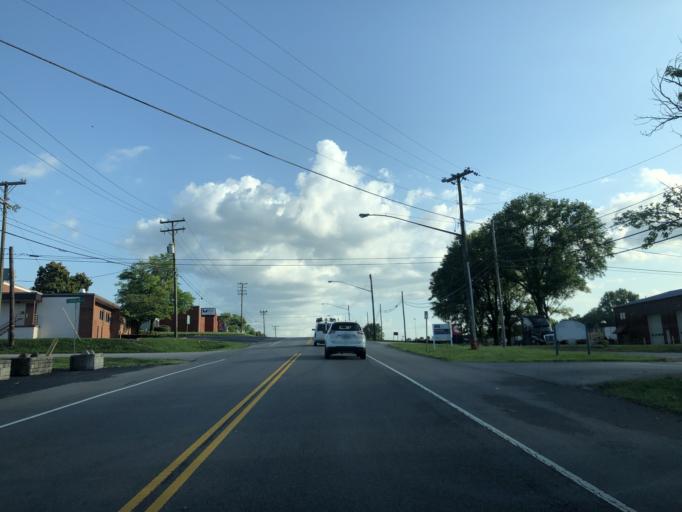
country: US
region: Tennessee
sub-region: Davidson County
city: Nashville
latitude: 36.1395
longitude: -86.7230
